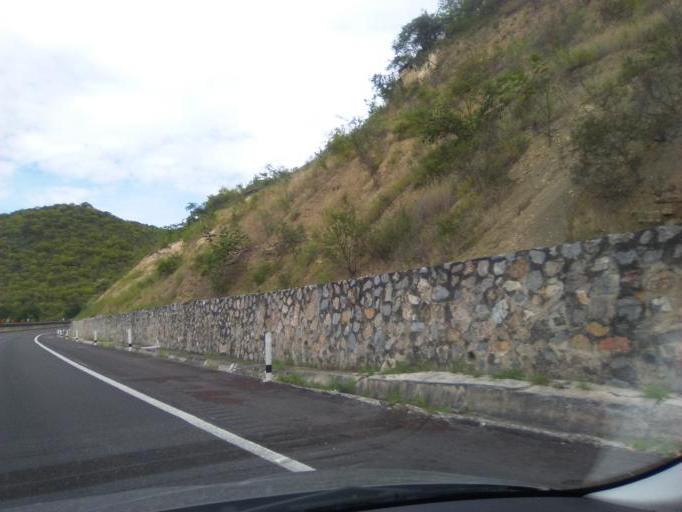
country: MX
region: Guerrero
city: Huitziltepec
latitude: 17.7112
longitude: -99.5095
